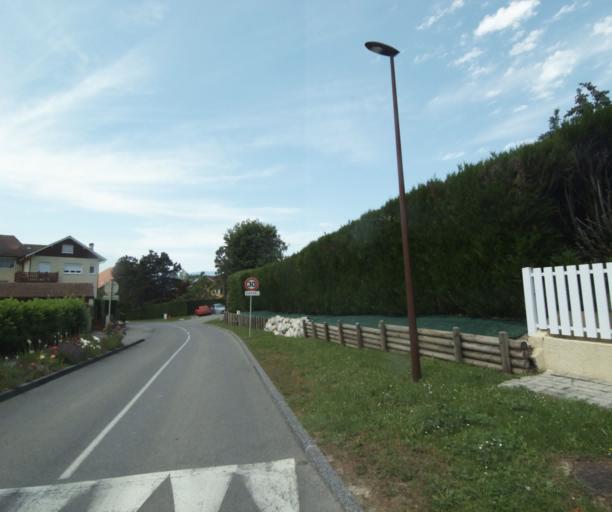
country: FR
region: Rhone-Alpes
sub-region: Departement de la Haute-Savoie
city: Messery
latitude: 46.3531
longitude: 6.3116
